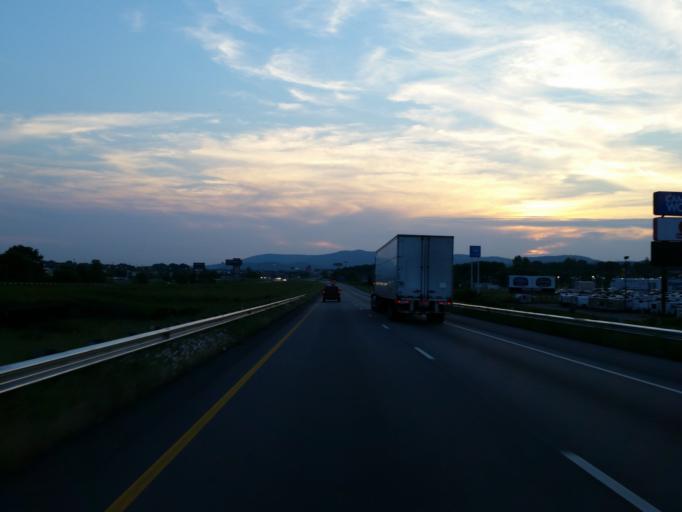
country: US
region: Alabama
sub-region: Calhoun County
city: Oxford
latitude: 33.6114
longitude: -85.7721
